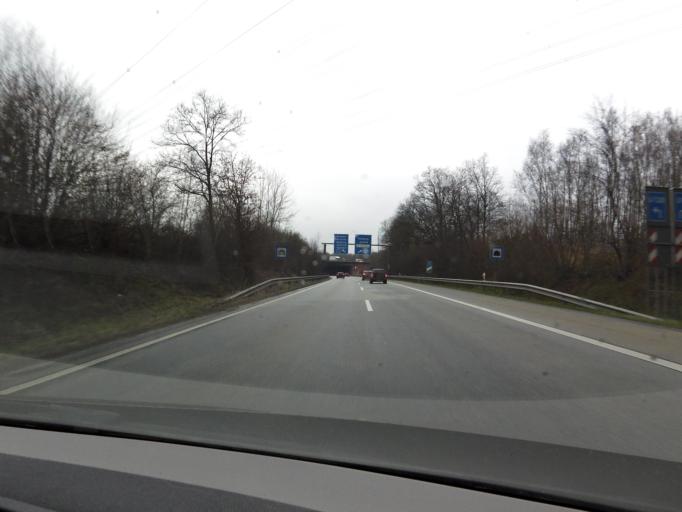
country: DE
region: Schleswig-Holstein
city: Barsbuettel
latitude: 53.5610
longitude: 10.1762
